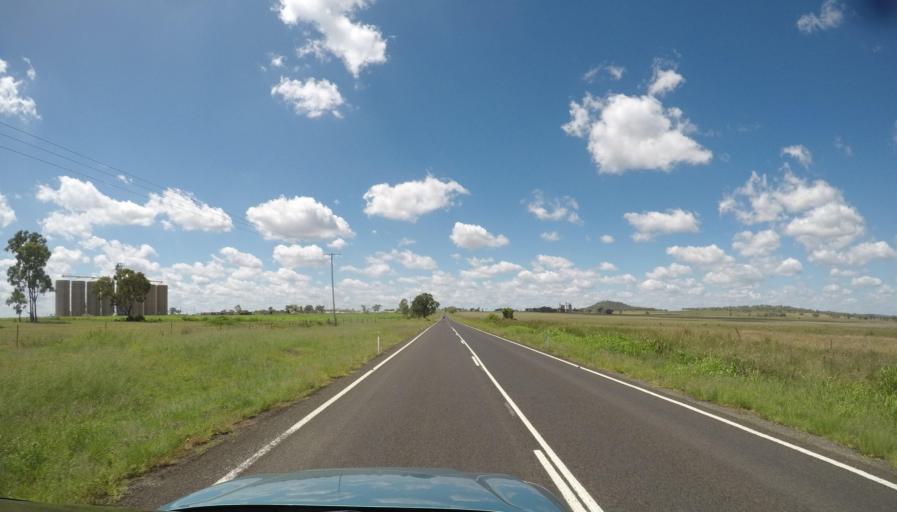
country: AU
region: Queensland
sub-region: Toowoomba
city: Oakey
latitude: -27.5318
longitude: 151.6138
